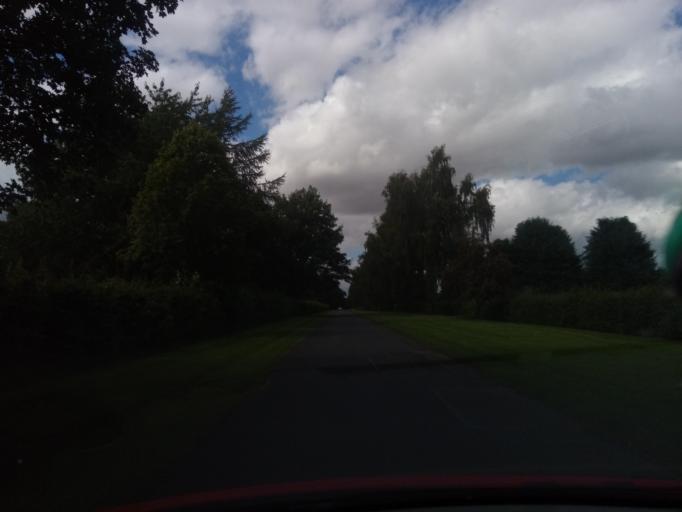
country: GB
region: Scotland
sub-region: The Scottish Borders
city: Coldstream
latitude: 55.6507
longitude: -2.2669
